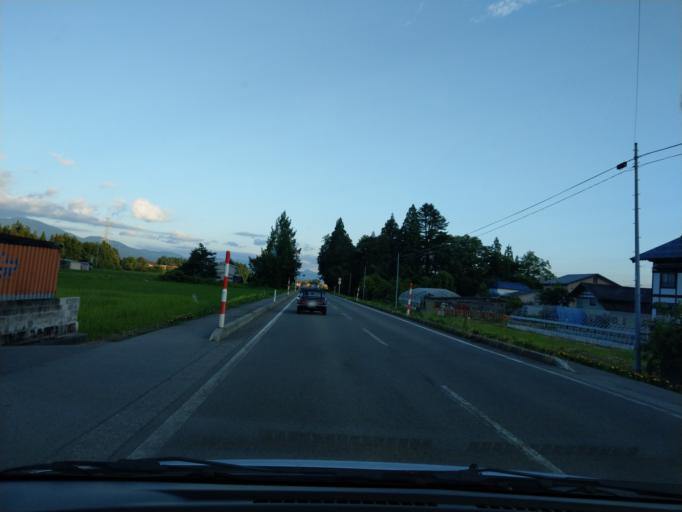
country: JP
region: Akita
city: Kakunodatemachi
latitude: 39.6697
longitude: 140.5676
